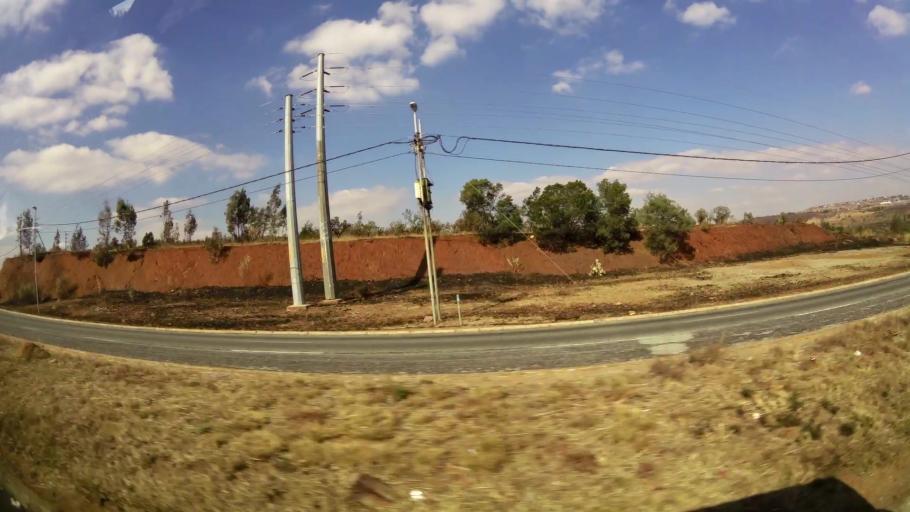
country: ZA
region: Gauteng
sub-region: West Rand District Municipality
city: Krugersdorp
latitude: -26.0639
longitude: 27.8063
